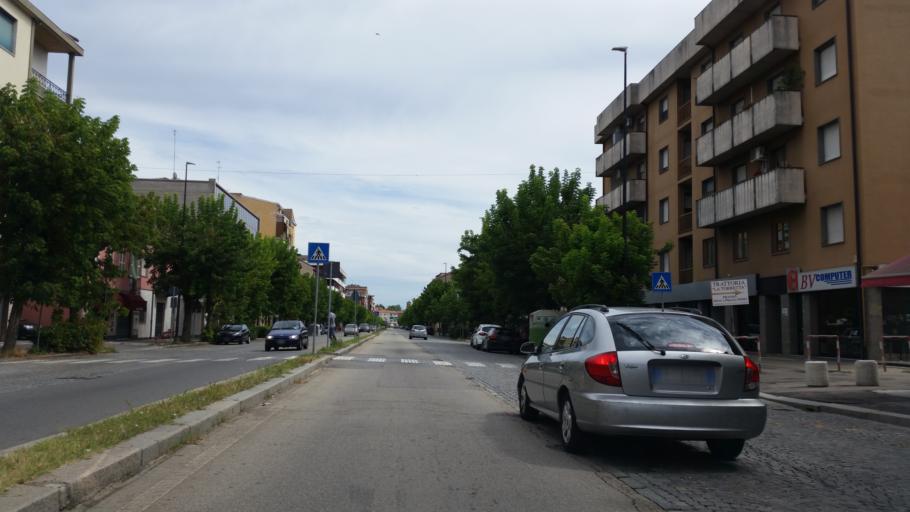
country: IT
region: Piedmont
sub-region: Provincia di Asti
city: Asti
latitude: 44.9047
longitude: 8.1874
